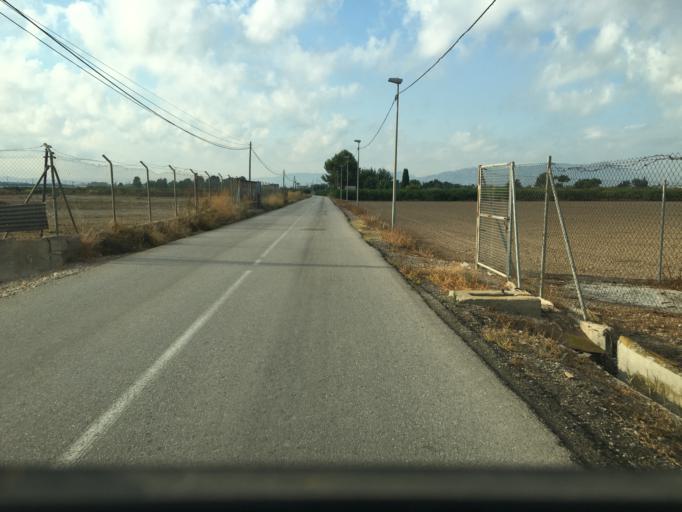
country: ES
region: Murcia
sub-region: Murcia
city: Santomera
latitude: 38.0511
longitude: -1.0406
